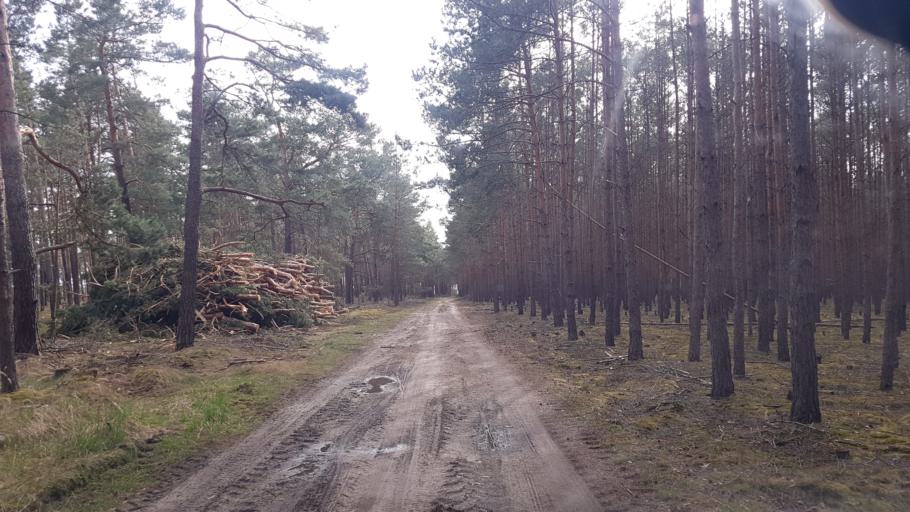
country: DE
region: Brandenburg
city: Schlieben
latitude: 51.6754
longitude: 13.4378
